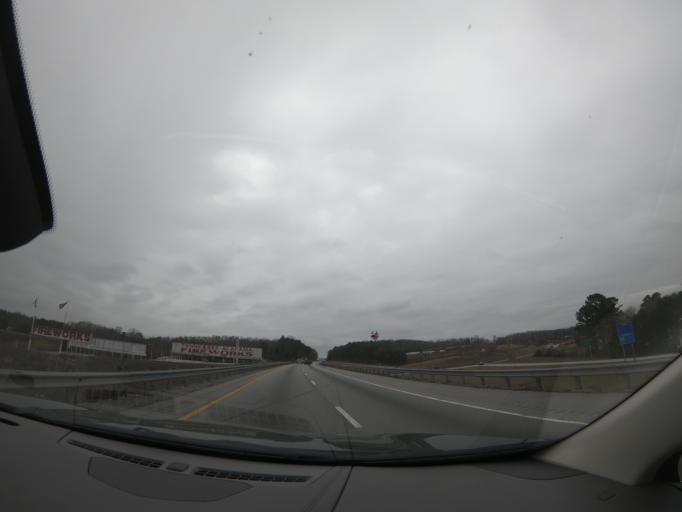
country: US
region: Tennessee
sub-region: Marion County
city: Jasper
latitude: 35.0326
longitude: -85.5804
